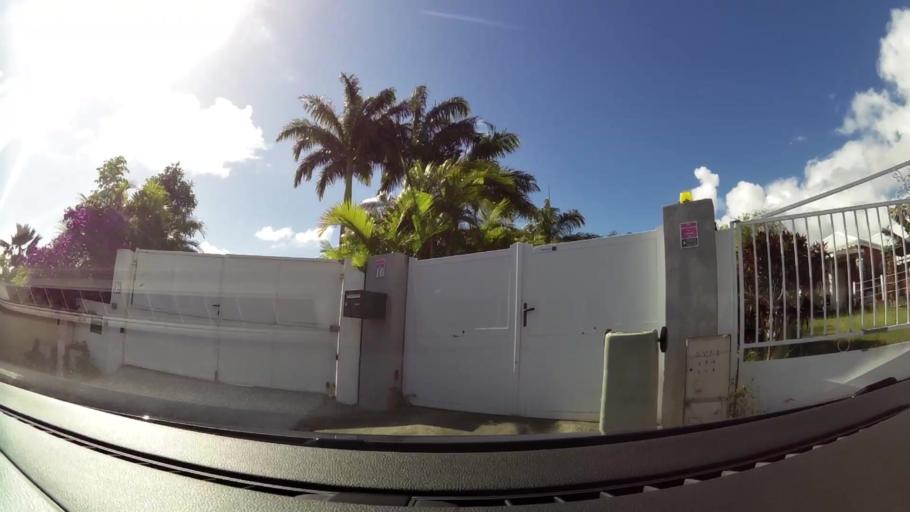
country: GP
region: Guadeloupe
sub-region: Guadeloupe
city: Sainte-Anne
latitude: 16.2368
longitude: -61.3801
